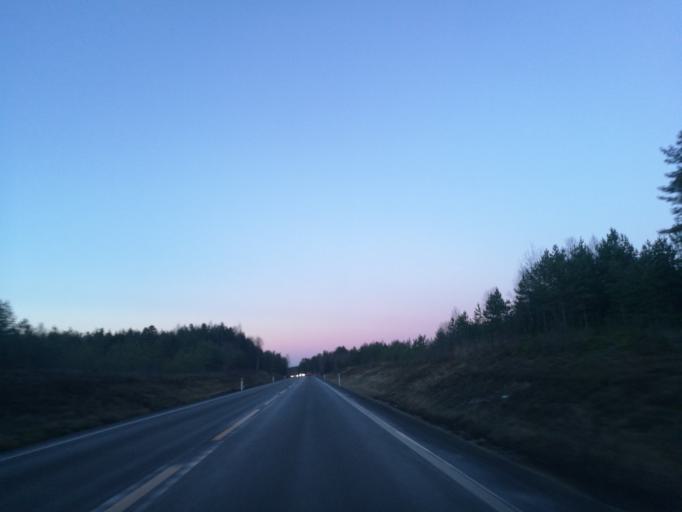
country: NO
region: Hedmark
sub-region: Eidskog
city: Skotterud
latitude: 60.0516
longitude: 12.1231
